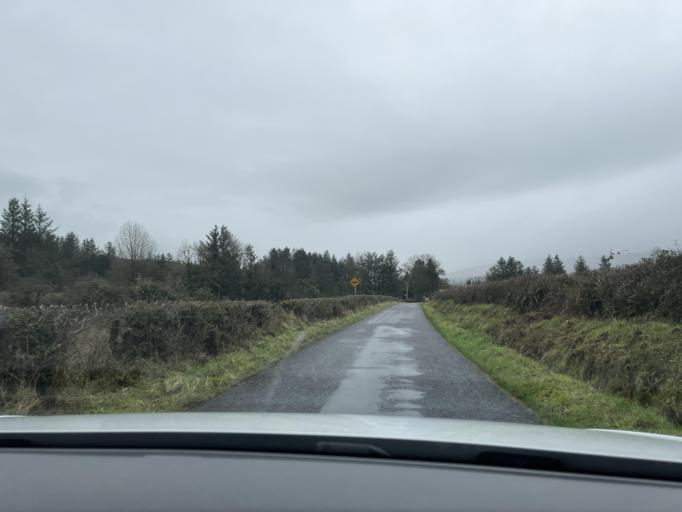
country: IE
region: Connaught
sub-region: County Leitrim
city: Manorhamilton
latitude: 54.2944
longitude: -8.0619
